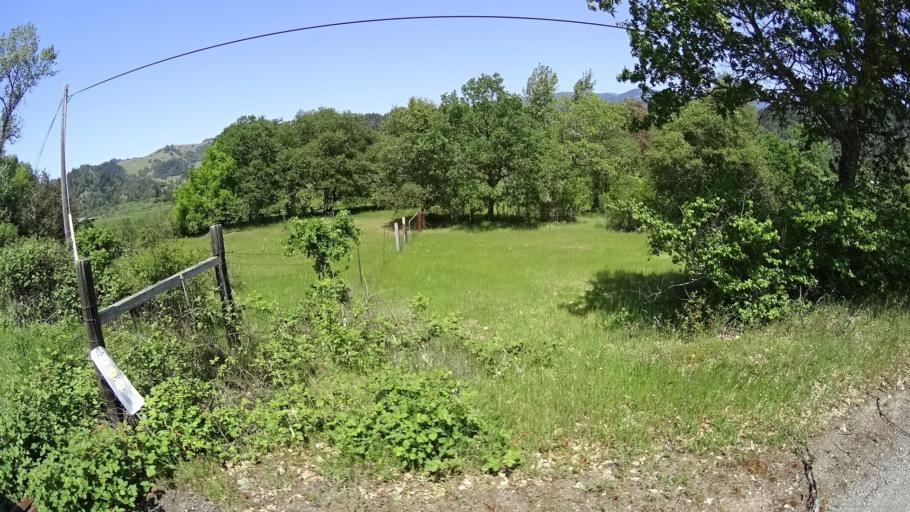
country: US
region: California
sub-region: Humboldt County
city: Redway
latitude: 40.2174
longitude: -123.6433
